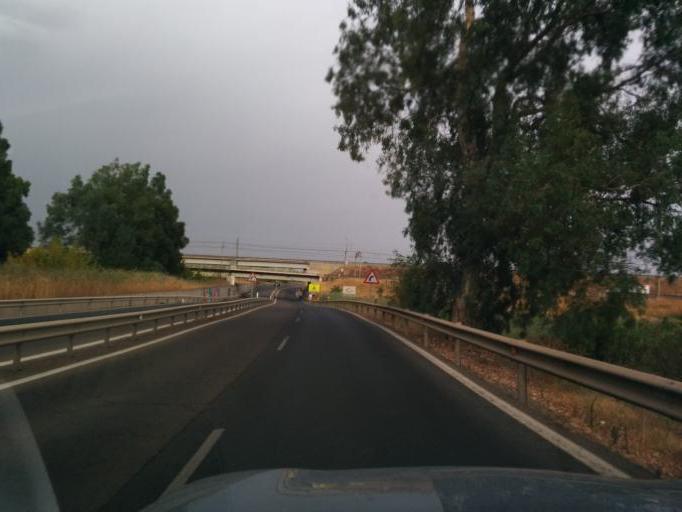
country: ES
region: Andalusia
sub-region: Provincia de Sevilla
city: Sevilla
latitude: 37.4240
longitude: -5.9528
